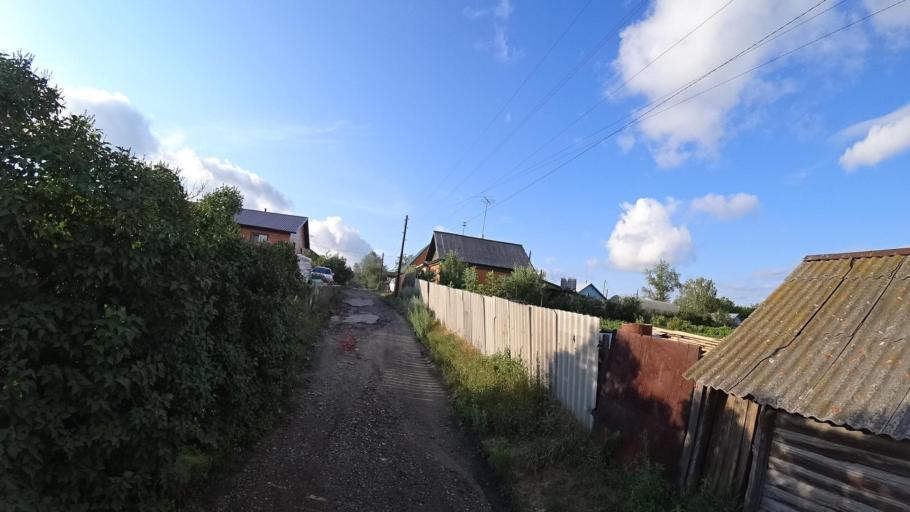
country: RU
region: Sverdlovsk
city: Kamyshlov
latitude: 56.8476
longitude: 62.6712
